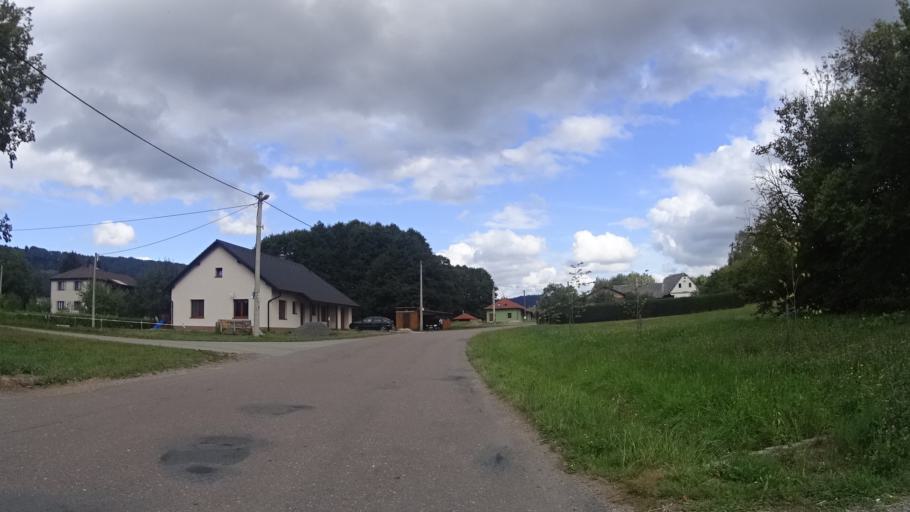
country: CZ
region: Pardubicky
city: Dolni Cermna
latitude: 49.9370
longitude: 16.5297
